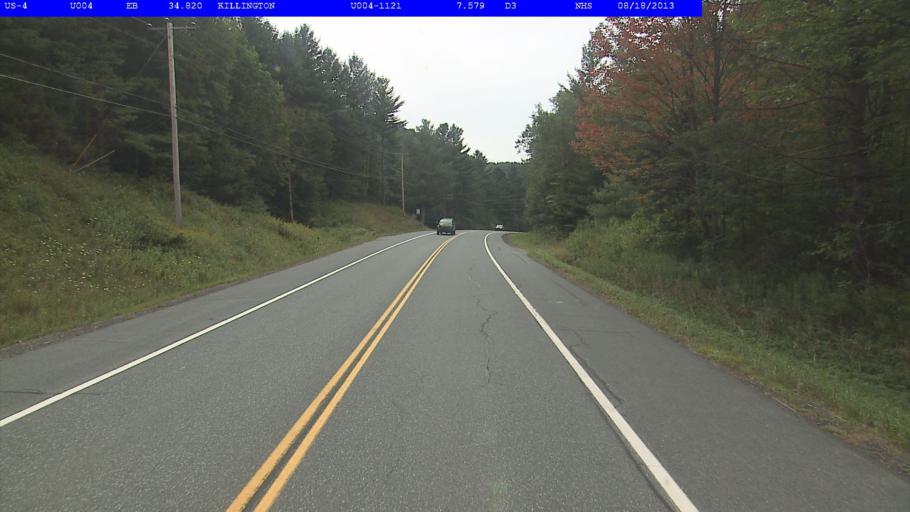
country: US
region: Vermont
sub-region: Rutland County
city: Rutland
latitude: 43.6129
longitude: -72.7538
